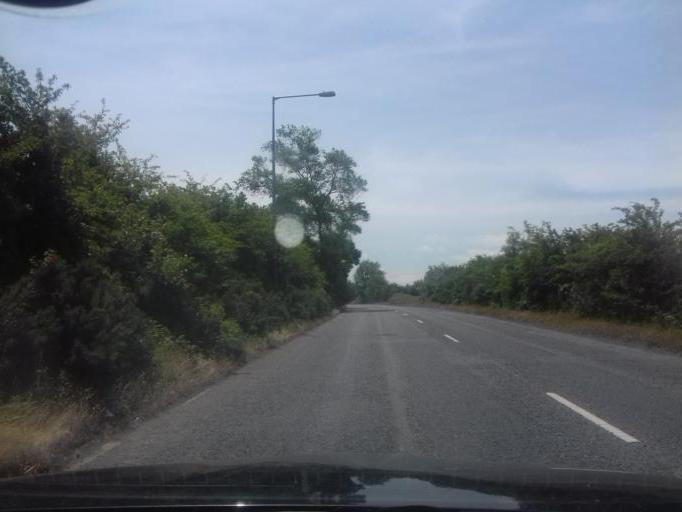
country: IE
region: Leinster
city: Balrothery
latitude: 53.5582
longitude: -6.2110
